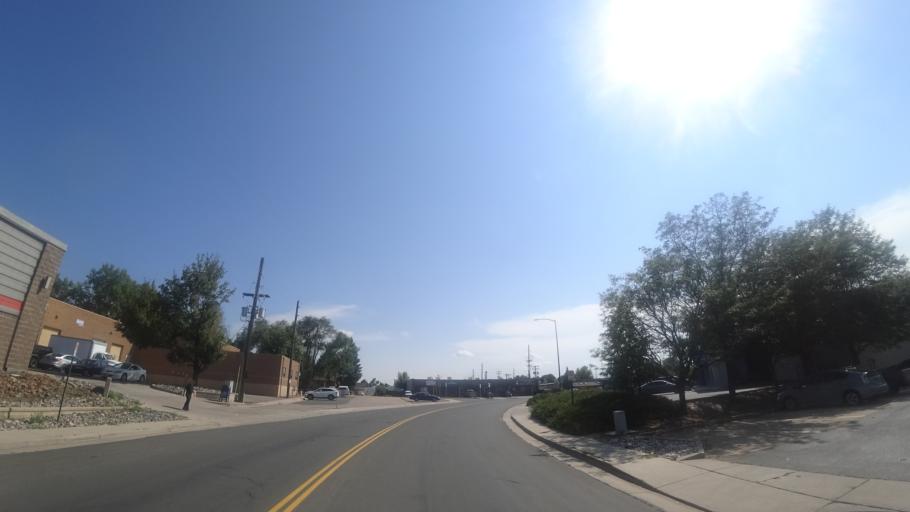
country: US
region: Colorado
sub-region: Arapahoe County
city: Englewood
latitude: 39.6339
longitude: -105.0046
